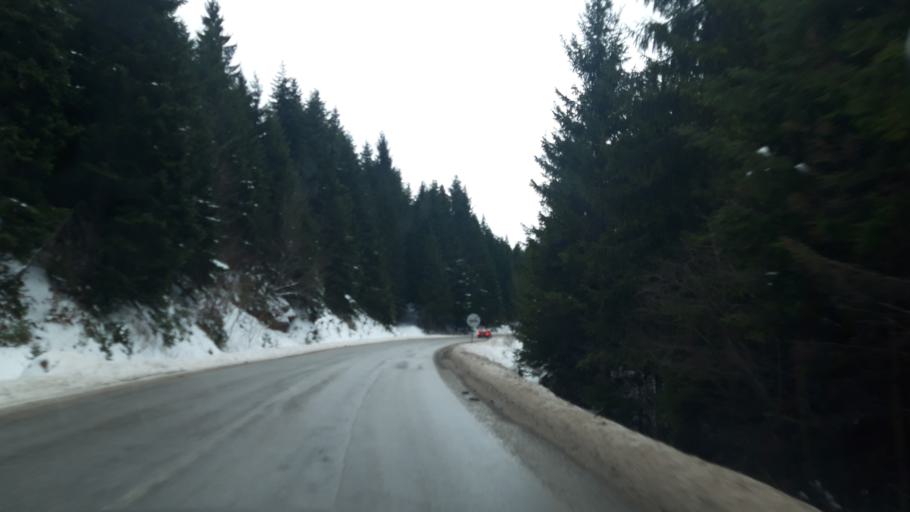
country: BA
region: Republika Srpska
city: Pale
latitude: 43.9136
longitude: 18.6453
